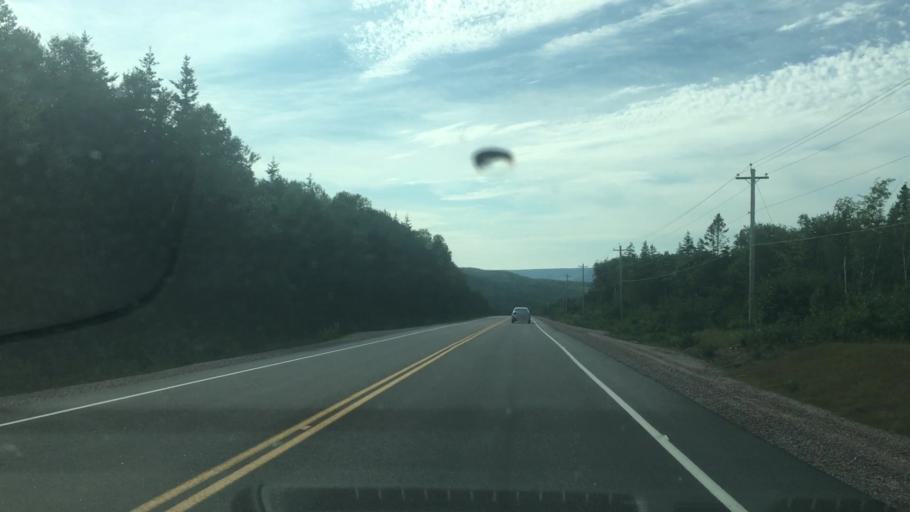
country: CA
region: Nova Scotia
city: Sydney Mines
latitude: 46.8551
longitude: -60.4441
